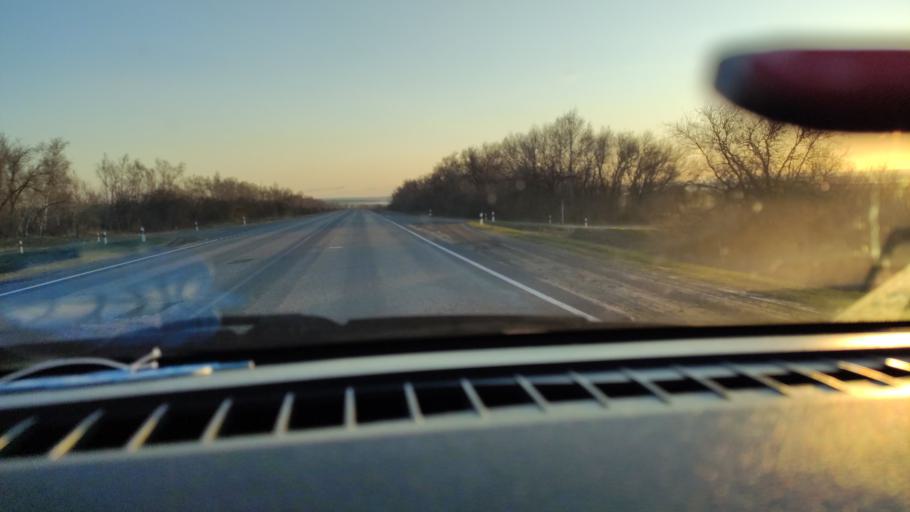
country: RU
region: Saratov
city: Sinodskoye
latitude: 51.9498
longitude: 46.6071
